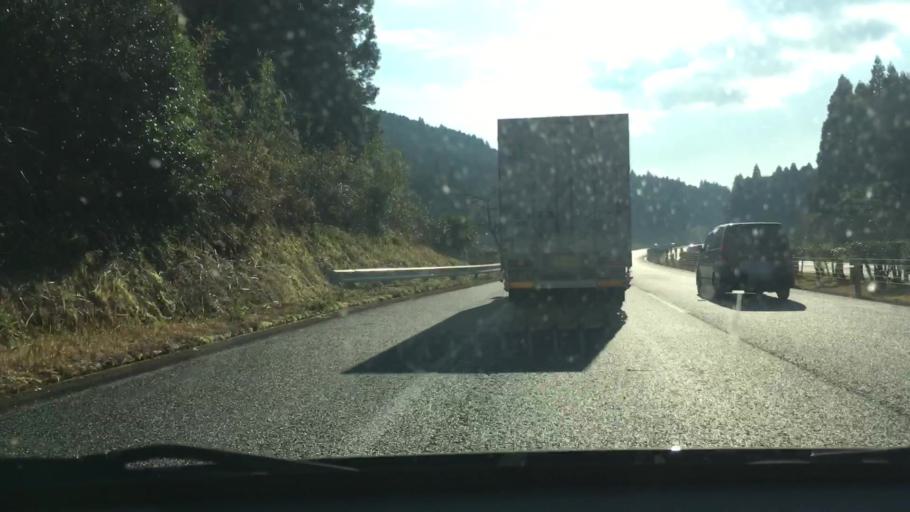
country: JP
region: Kagoshima
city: Okuchi-shinohara
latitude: 31.9614
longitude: 130.7440
